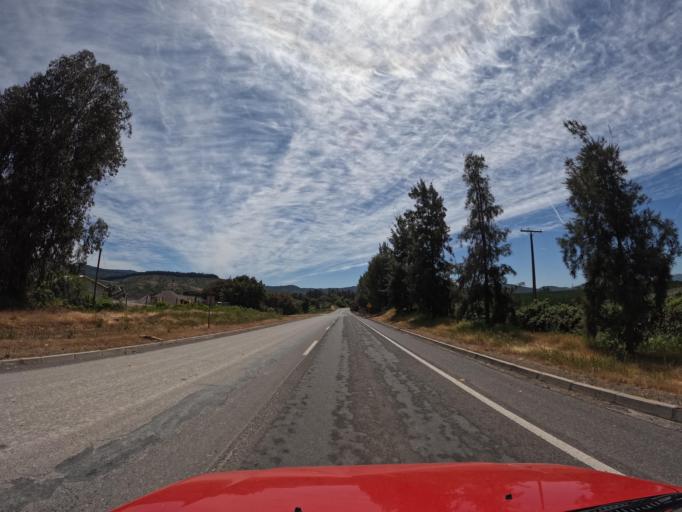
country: CL
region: Maule
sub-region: Provincia de Talca
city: Talca
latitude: -35.2949
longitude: -71.5291
